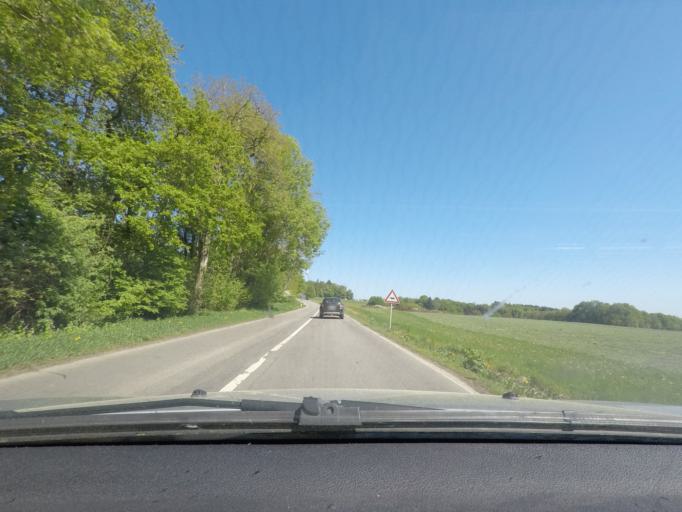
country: BE
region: Wallonia
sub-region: Province de Namur
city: Rochefort
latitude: 50.2127
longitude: 5.1483
